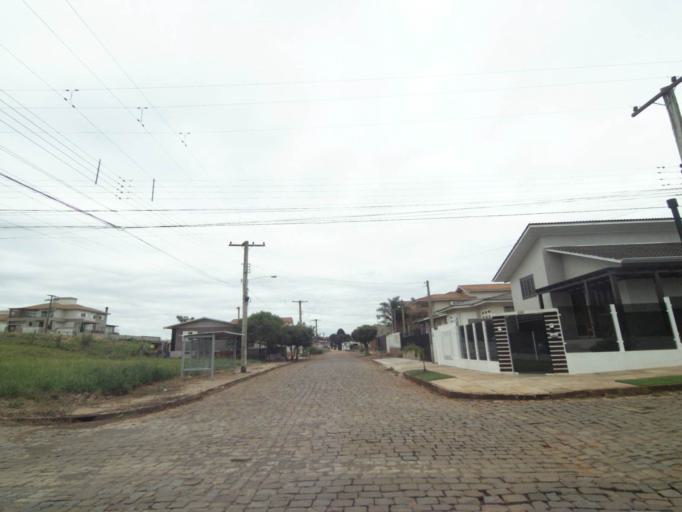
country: BR
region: Rio Grande do Sul
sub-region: Lagoa Vermelha
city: Lagoa Vermelha
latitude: -28.2160
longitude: -51.5311
